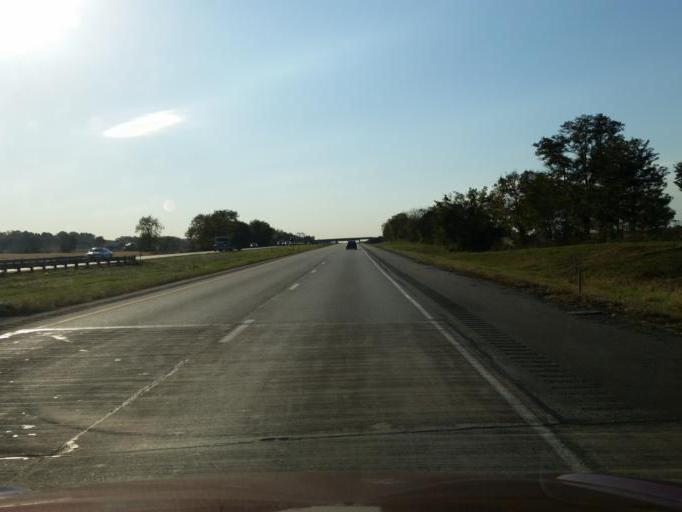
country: US
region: Pennsylvania
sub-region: Lancaster County
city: Mount Joy
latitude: 40.1294
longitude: -76.5010
